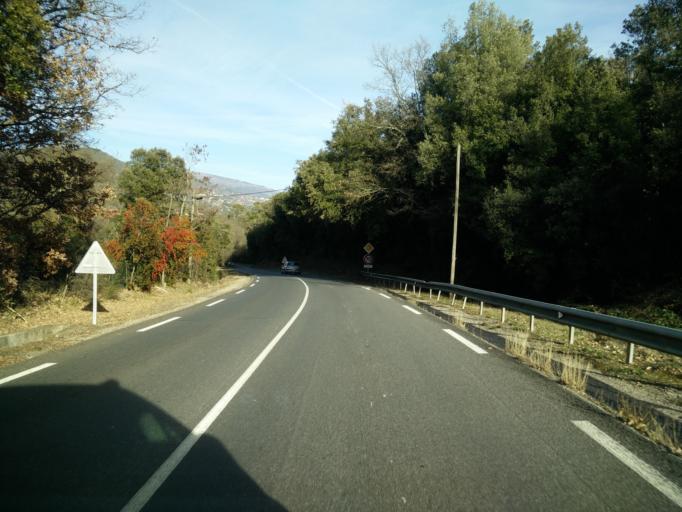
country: FR
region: Provence-Alpes-Cote d'Azur
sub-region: Departement des Alpes-Maritimes
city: Le Tignet
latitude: 43.6126
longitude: 6.8190
